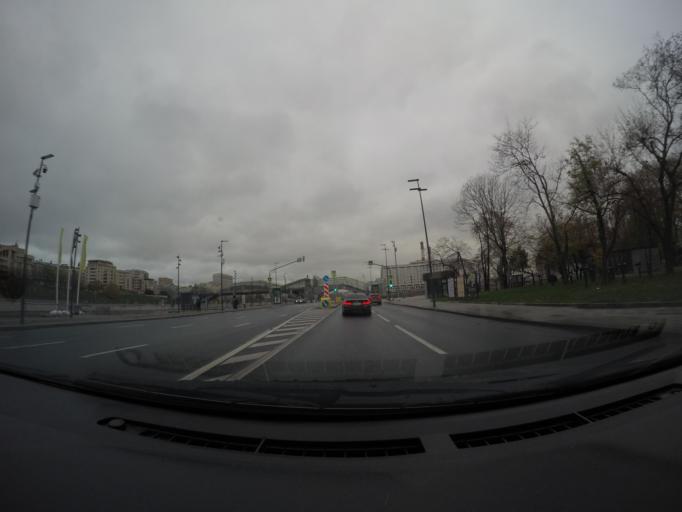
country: RU
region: Moskovskaya
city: Dorogomilovo
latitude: 55.7438
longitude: 37.5713
